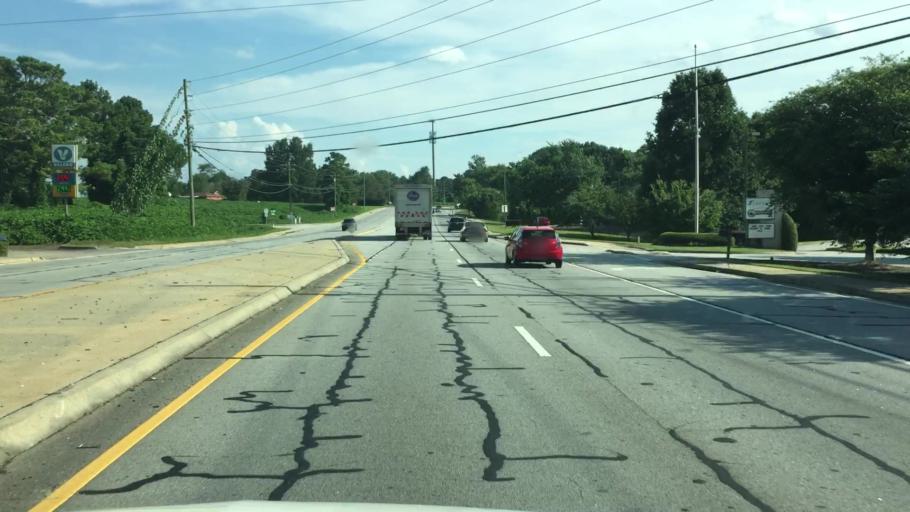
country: US
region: Georgia
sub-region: Gwinnett County
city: Snellville
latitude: 33.7961
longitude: -84.0414
